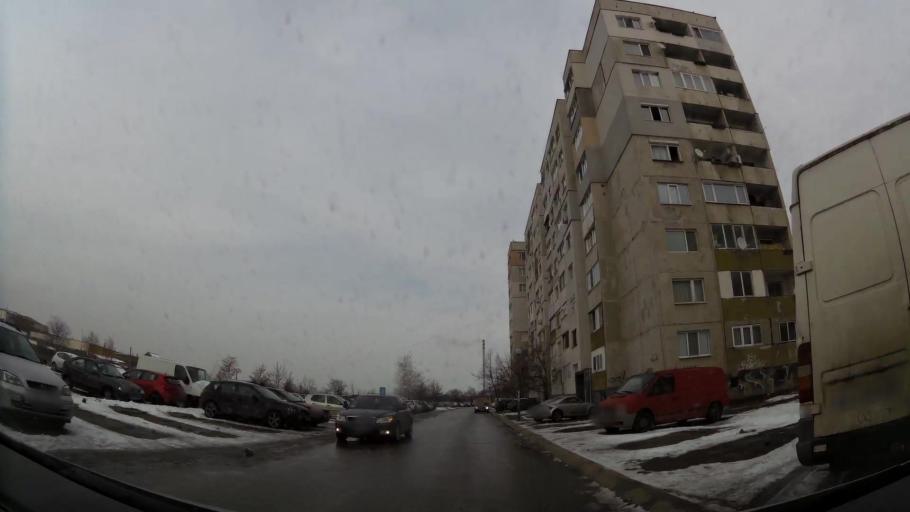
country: BG
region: Sofia-Capital
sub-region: Stolichna Obshtina
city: Sofia
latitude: 42.7127
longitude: 23.3751
